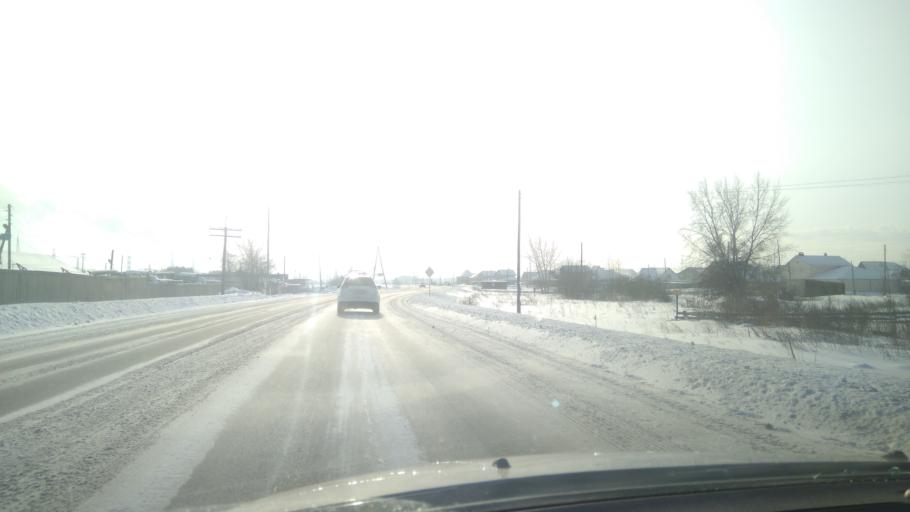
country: RU
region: Sverdlovsk
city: Sukhoy Log
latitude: 56.8885
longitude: 62.0423
